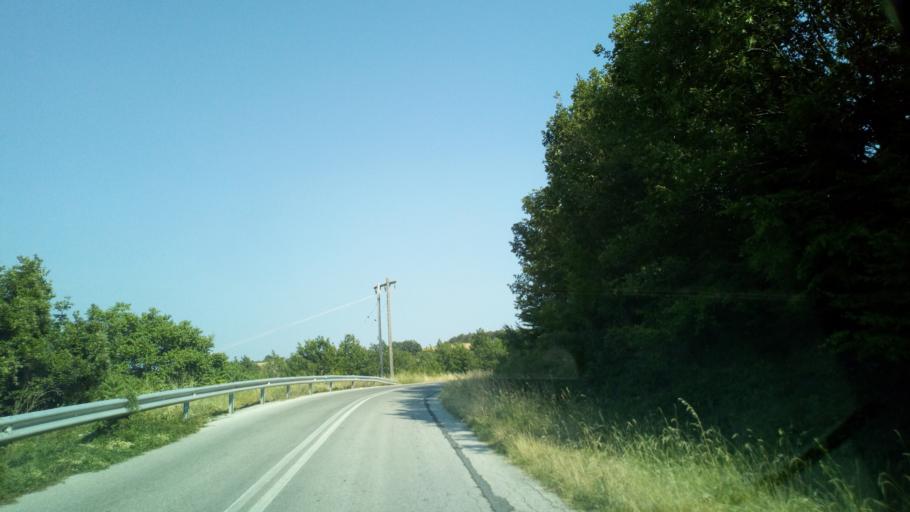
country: GR
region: Central Macedonia
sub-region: Nomos Chalkidikis
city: Polygyros
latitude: 40.4886
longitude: 23.3988
